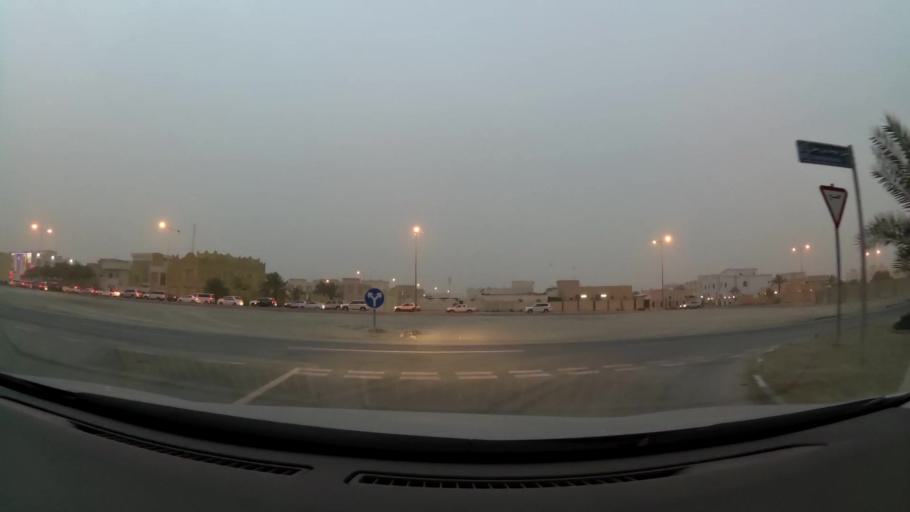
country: QA
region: Baladiyat ad Dawhah
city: Doha
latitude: 25.2304
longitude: 51.4909
